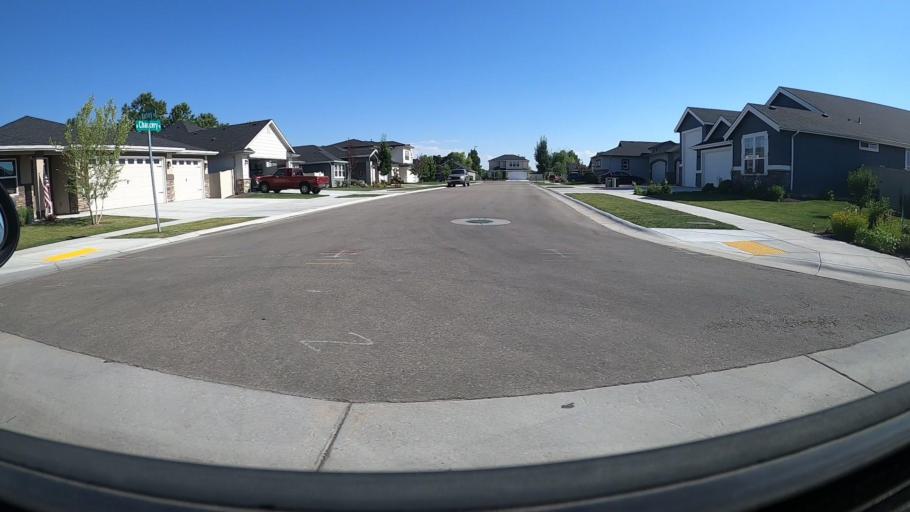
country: US
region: Idaho
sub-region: Ada County
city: Meridian
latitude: 43.6317
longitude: -116.3689
